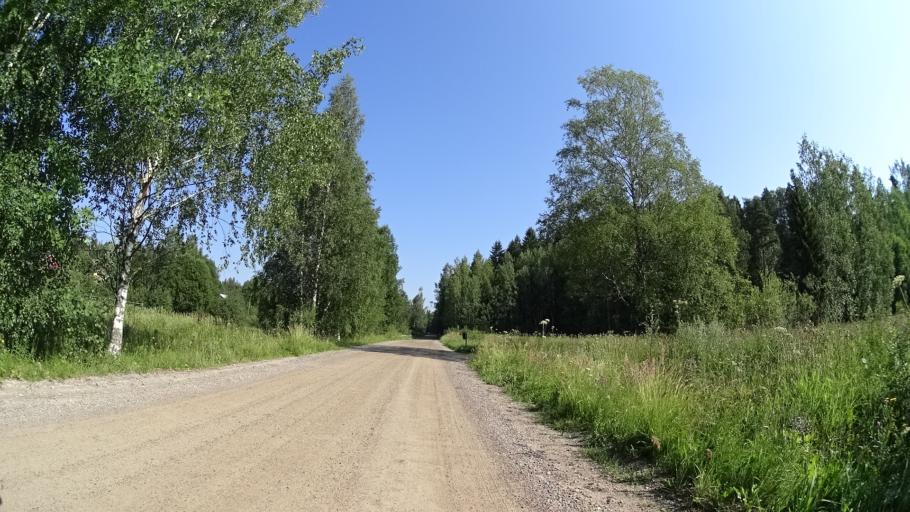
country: FI
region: Uusimaa
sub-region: Helsinki
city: Kerava
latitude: 60.3636
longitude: 25.1238
